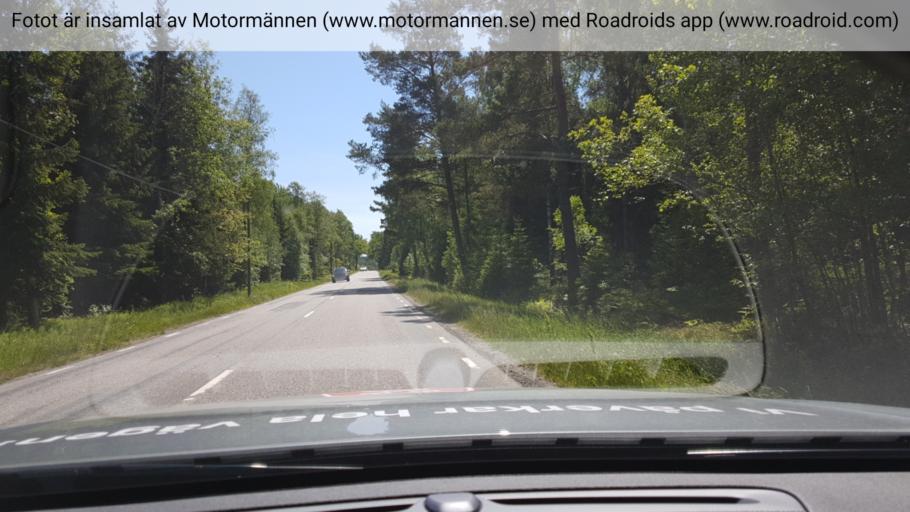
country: SE
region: Stockholm
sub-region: Haninge Kommun
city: Haninge
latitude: 59.1195
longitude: 18.1869
